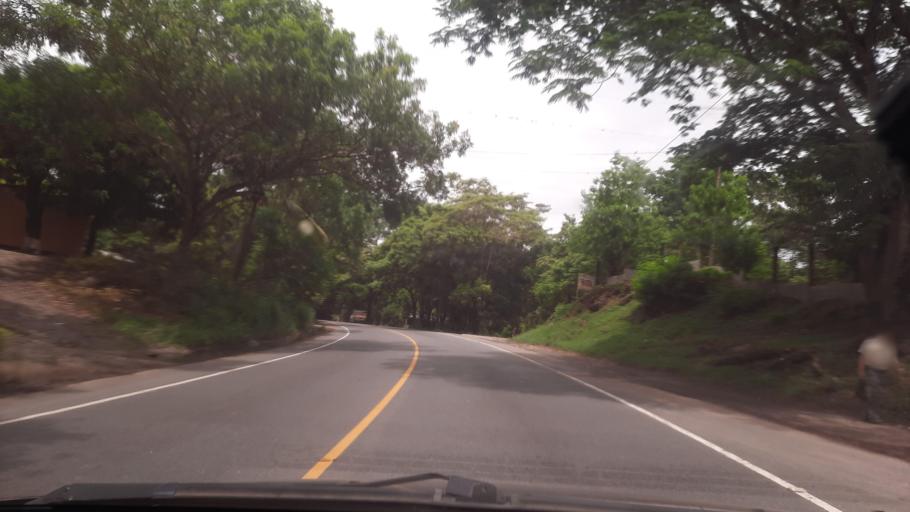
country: GT
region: Izabal
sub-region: Municipio de Los Amates
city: Los Amates
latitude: 15.2154
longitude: -89.2362
